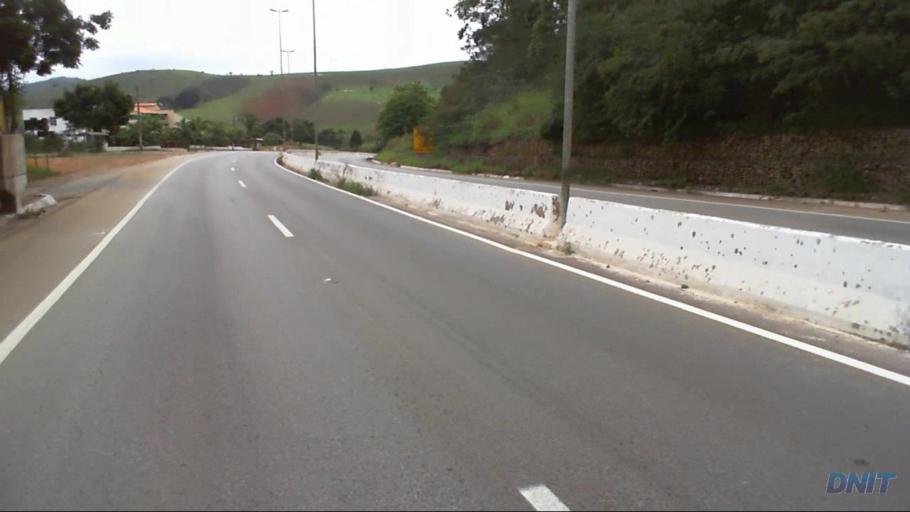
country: BR
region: Minas Gerais
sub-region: Nova Era
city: Nova Era
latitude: -19.7617
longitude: -43.0433
